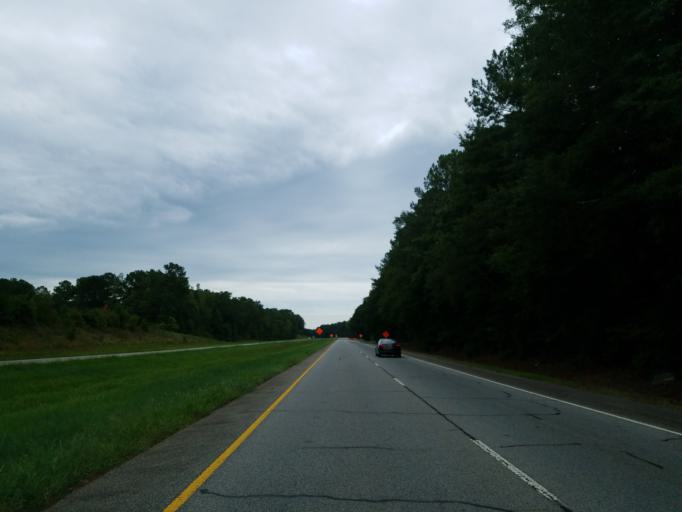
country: US
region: Georgia
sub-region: Spalding County
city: East Griffin
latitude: 33.1556
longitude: -84.2533
